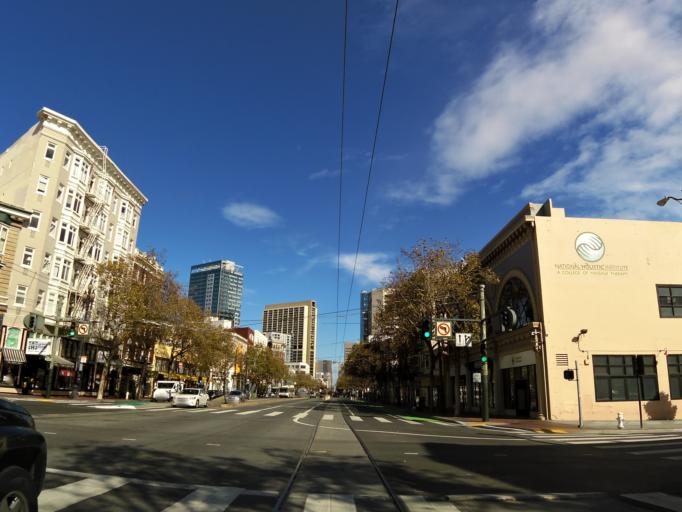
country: US
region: California
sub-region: San Francisco County
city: San Francisco
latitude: 37.7729
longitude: -122.4221
